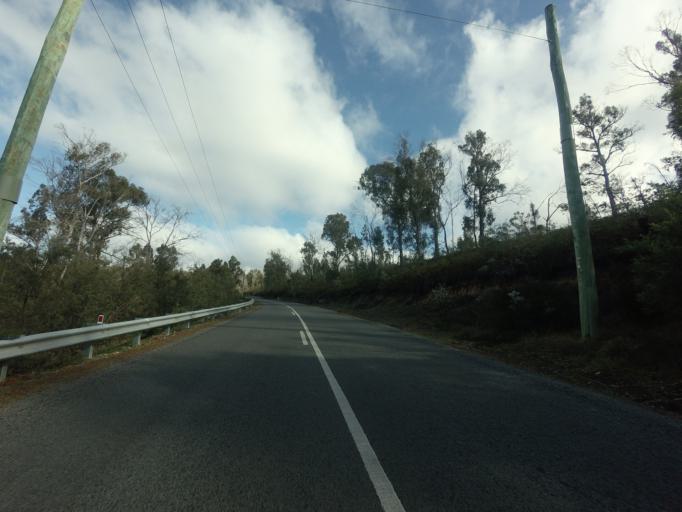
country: AU
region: Tasmania
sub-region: Derwent Valley
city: New Norfolk
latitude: -42.5421
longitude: 146.7193
